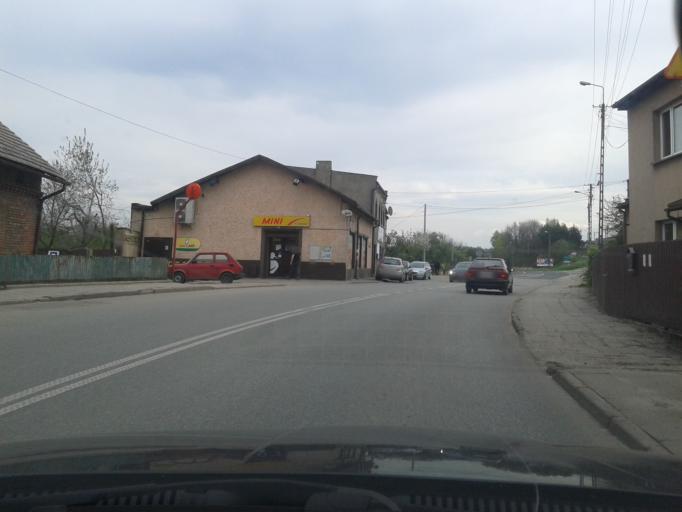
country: PL
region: Silesian Voivodeship
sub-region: Rybnik
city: Rybnik
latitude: 50.1188
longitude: 18.5233
